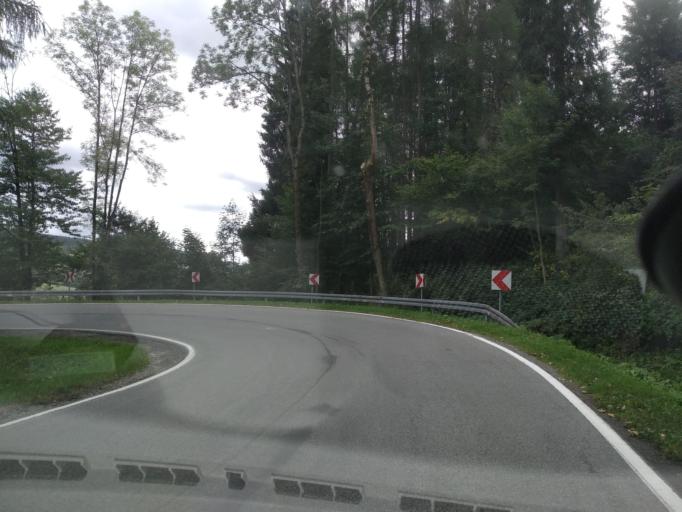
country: PL
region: Lesser Poland Voivodeship
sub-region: Powiat gorlicki
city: Sekowa
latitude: 49.5560
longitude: 21.2536
